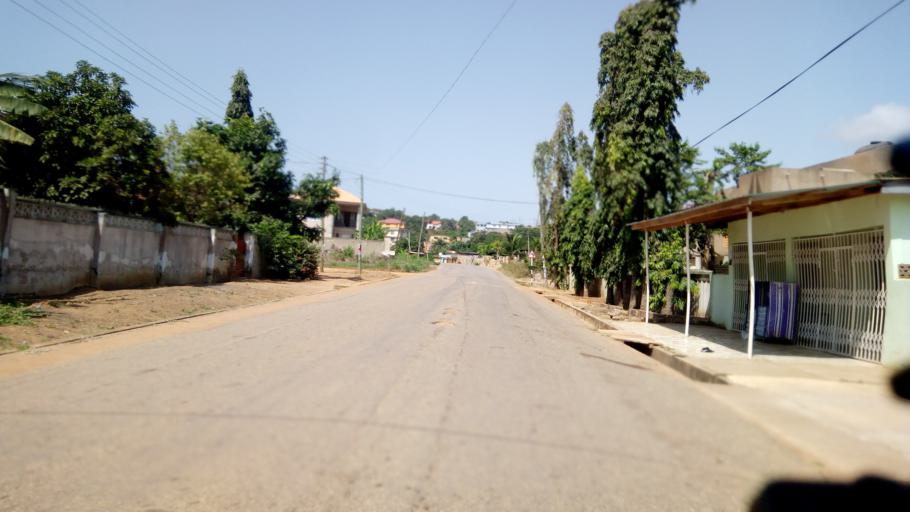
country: GH
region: Central
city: Cape Coast
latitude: 5.1131
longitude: -1.2708
